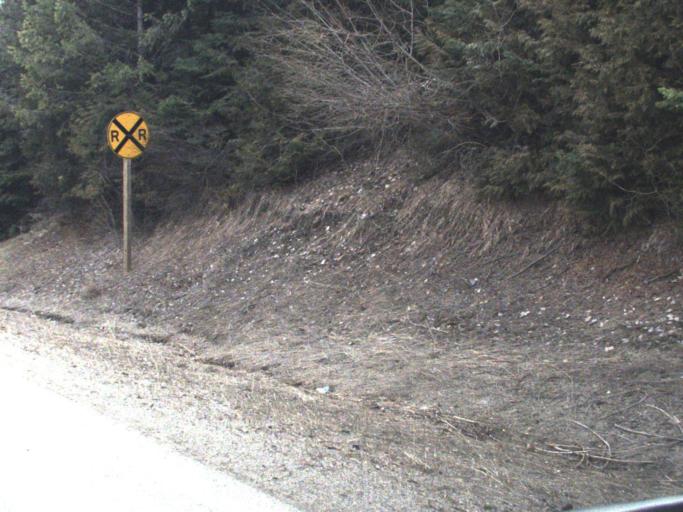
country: US
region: Washington
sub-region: Pend Oreille County
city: Newport
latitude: 48.2796
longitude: -117.2668
